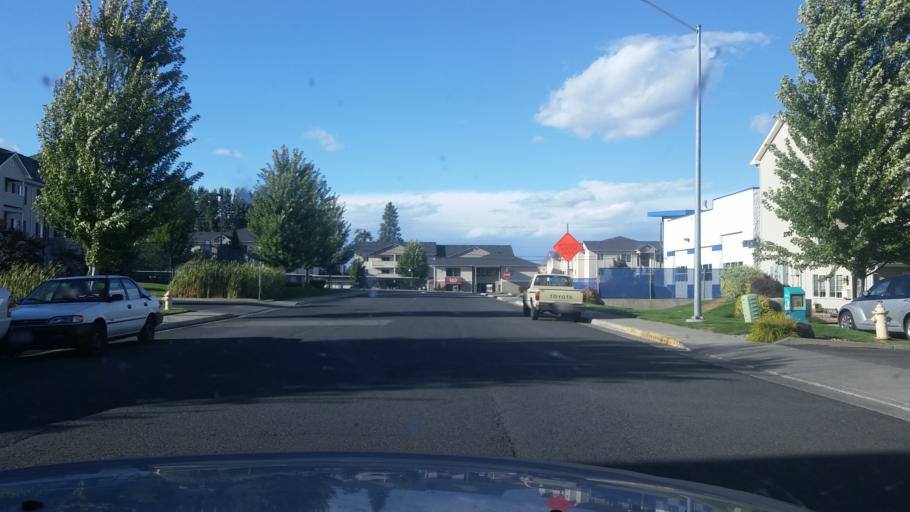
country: US
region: Washington
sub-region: Spokane County
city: Cheney
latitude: 47.5064
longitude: -117.5689
